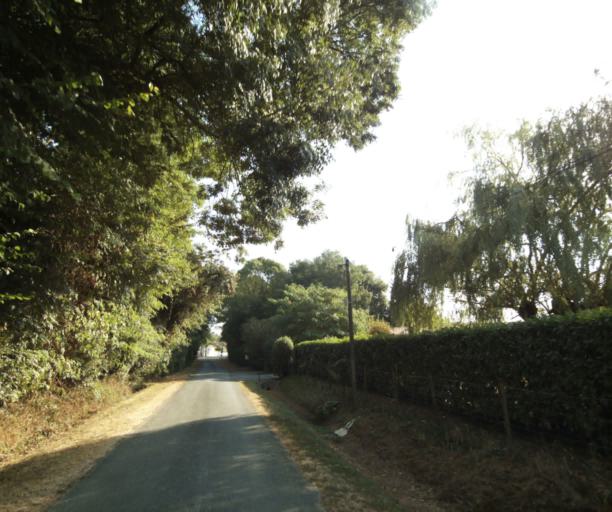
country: FR
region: Poitou-Charentes
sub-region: Departement de la Charente-Maritime
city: Cabariot
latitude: 45.9613
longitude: -0.8408
